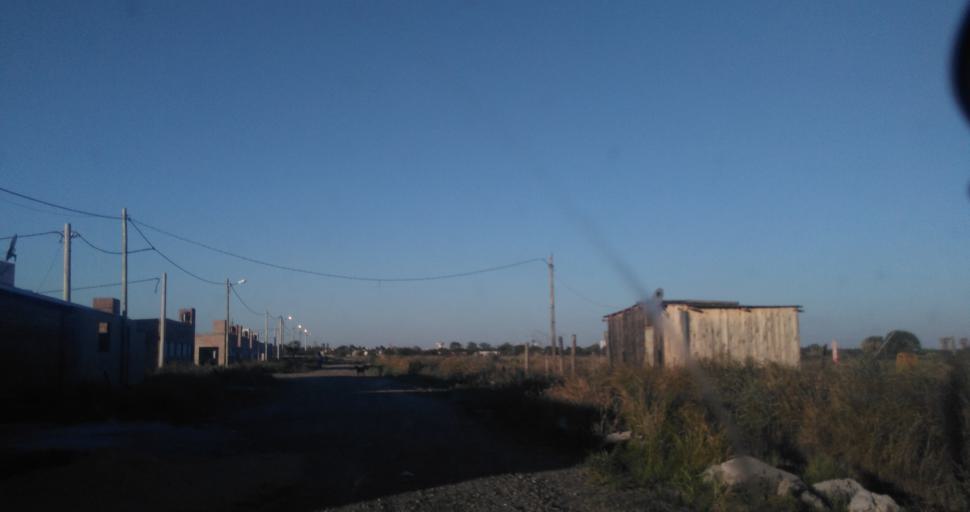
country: AR
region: Chaco
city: Resistencia
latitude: -27.4763
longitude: -59.0270
